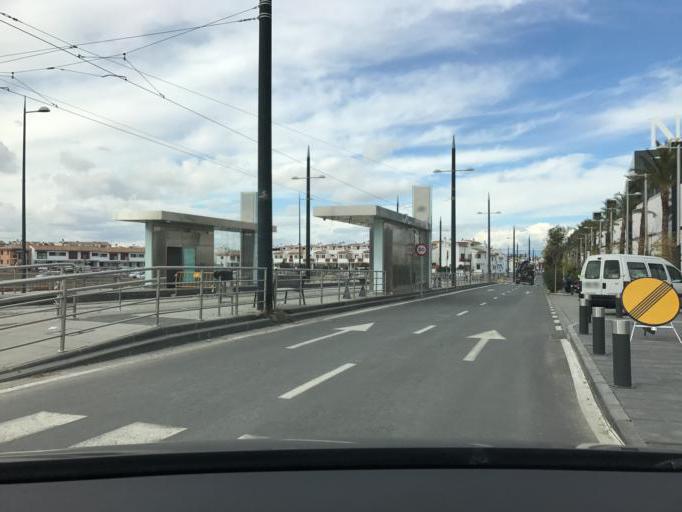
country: ES
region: Andalusia
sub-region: Provincia de Granada
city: Armilla
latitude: 37.1440
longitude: -3.6136
